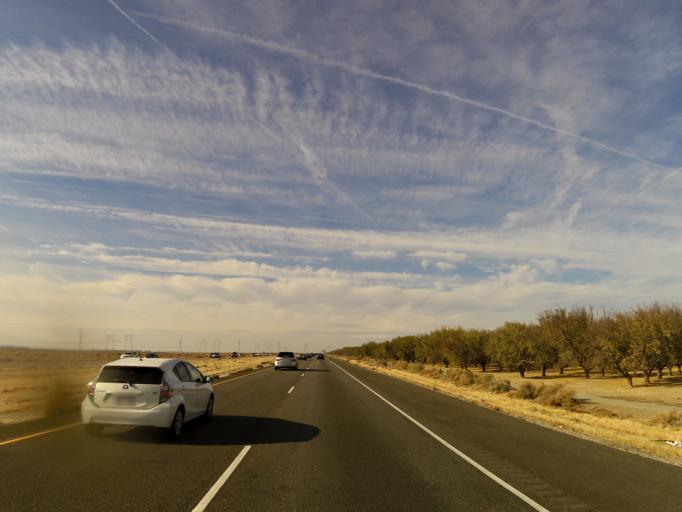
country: US
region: California
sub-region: Kern County
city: Buttonwillow
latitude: 35.4792
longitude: -119.5075
